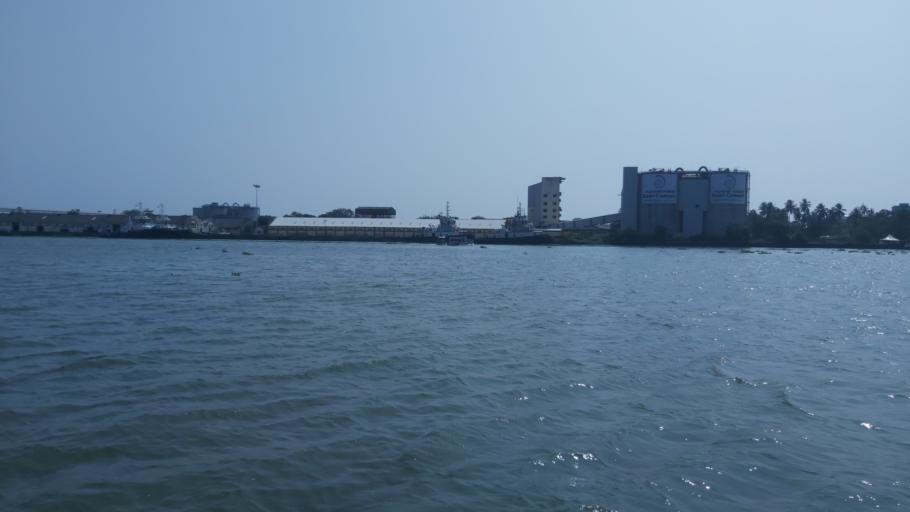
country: IN
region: Kerala
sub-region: Ernakulam
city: Cochin
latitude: 9.9719
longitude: 76.2650
